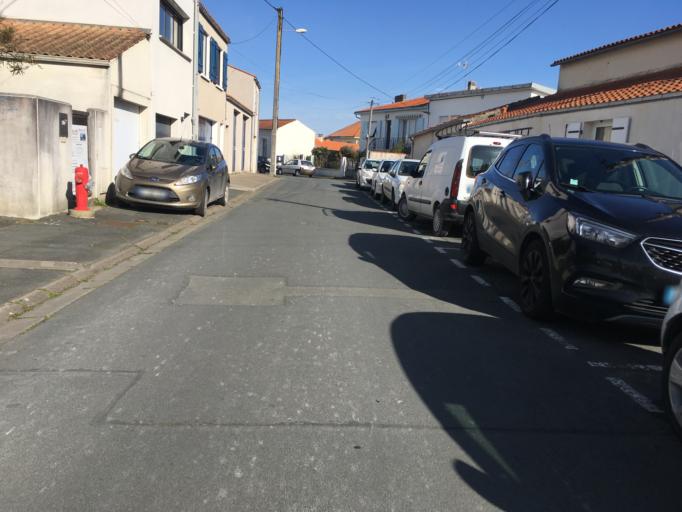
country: FR
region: Poitou-Charentes
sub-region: Departement de la Charente-Maritime
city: La Rochelle
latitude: 46.1466
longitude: -1.1424
